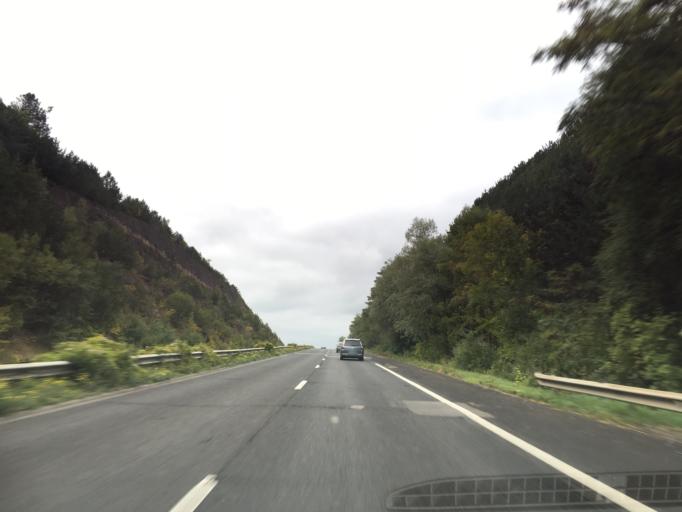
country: FR
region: Lorraine
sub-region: Departement de Meurthe-et-Moselle
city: Foug
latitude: 48.6736
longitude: 5.7725
